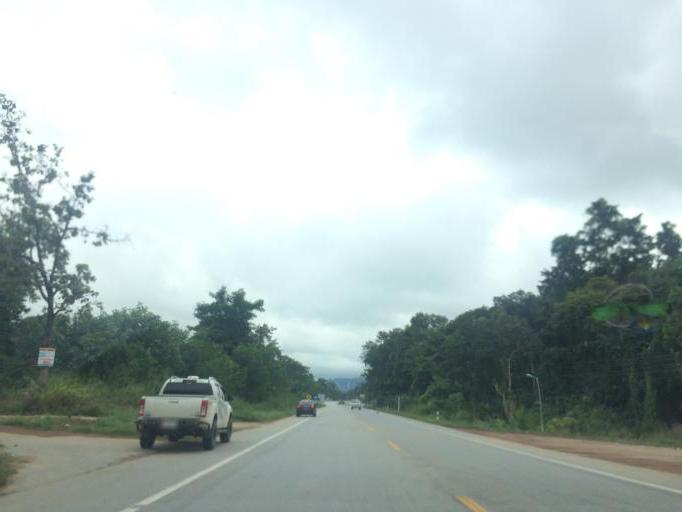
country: TH
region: Chiang Rai
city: Mae Lao
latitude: 19.7461
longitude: 99.6857
